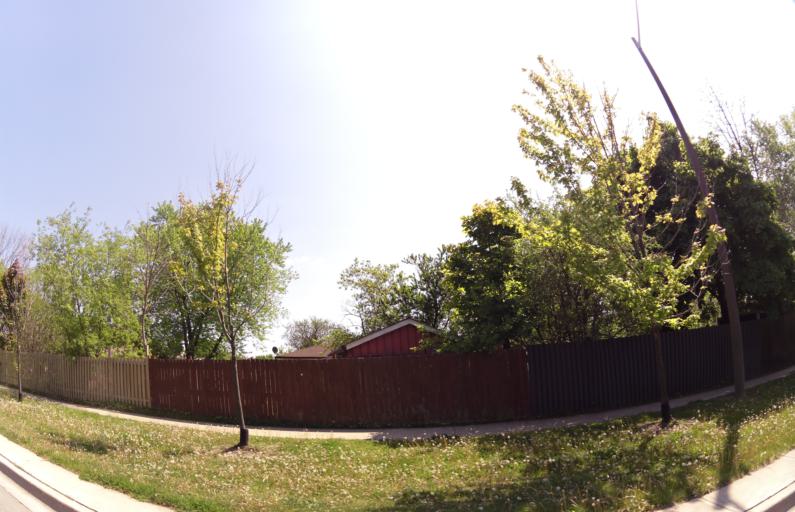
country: CA
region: Ontario
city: Mississauga
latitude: 43.5917
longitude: -79.6172
